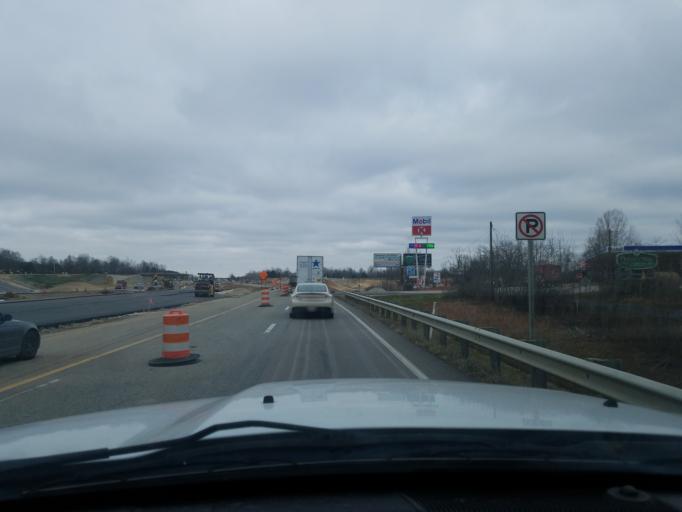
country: US
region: Indiana
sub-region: Monroe County
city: Bloomington
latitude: 39.2623
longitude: -86.5226
